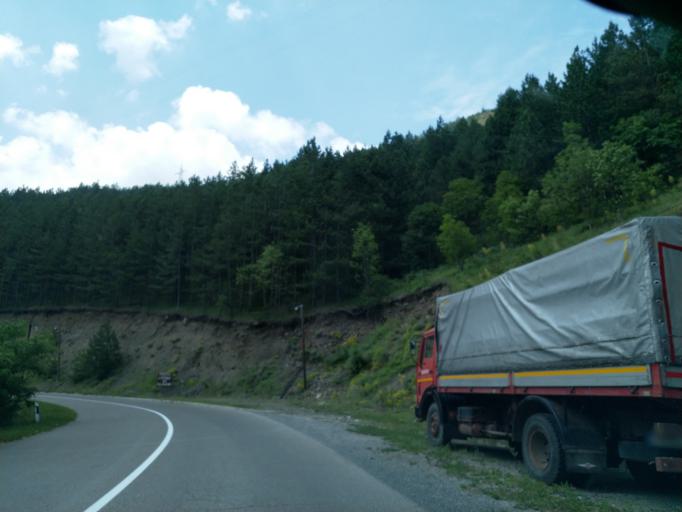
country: RS
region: Central Serbia
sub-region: Rasinski Okrug
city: Aleksandrovac
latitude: 43.3379
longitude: 20.9456
